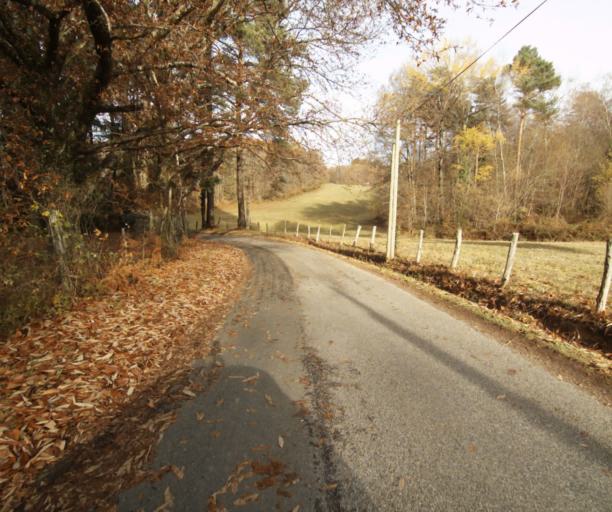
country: FR
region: Limousin
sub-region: Departement de la Correze
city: Sainte-Fortunade
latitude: 45.1805
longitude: 1.7424
